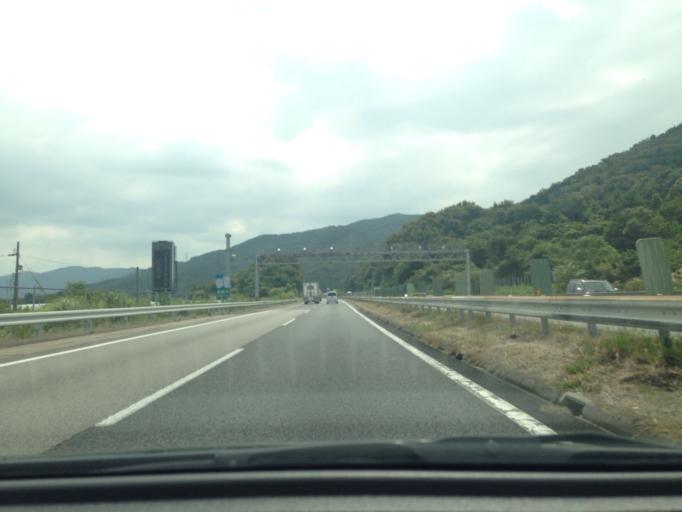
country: JP
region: Aichi
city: Shinshiro
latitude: 34.8438
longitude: 137.4891
